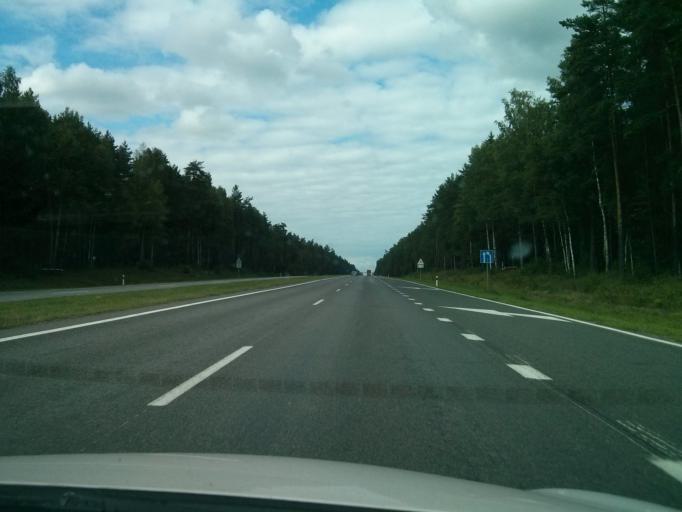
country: BY
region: Minsk
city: Zamostochcha
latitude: 53.8928
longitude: 27.9423
